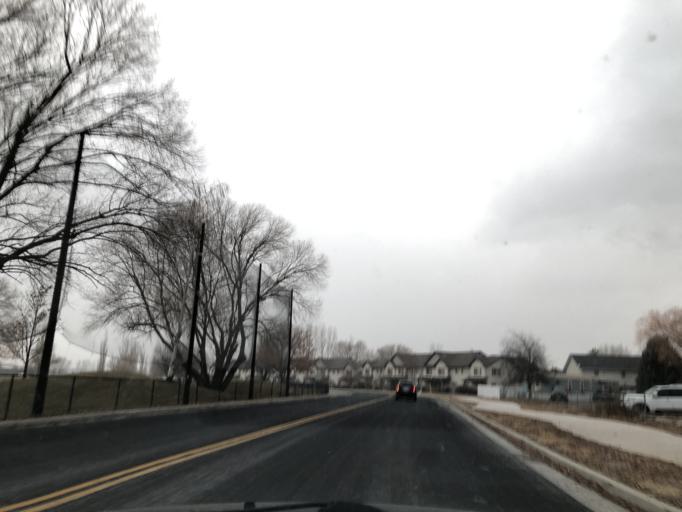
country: US
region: Utah
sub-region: Cache County
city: Logan
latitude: 41.7149
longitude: -111.8449
